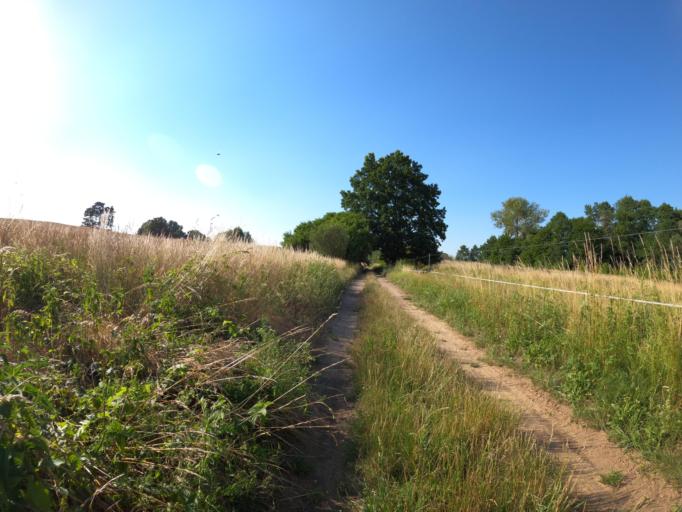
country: DE
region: Brandenburg
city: Gartz
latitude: 53.2301
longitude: 14.3680
